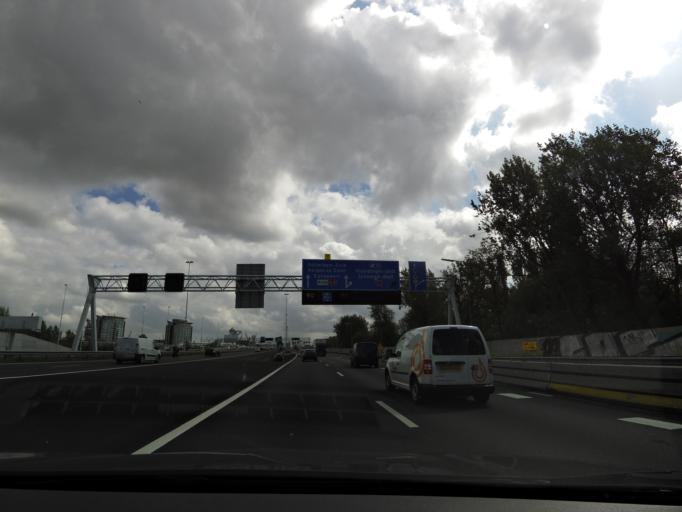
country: NL
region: South Holland
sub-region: Gemeente Schiedam
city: Schiedam
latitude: 51.9131
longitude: 4.3681
